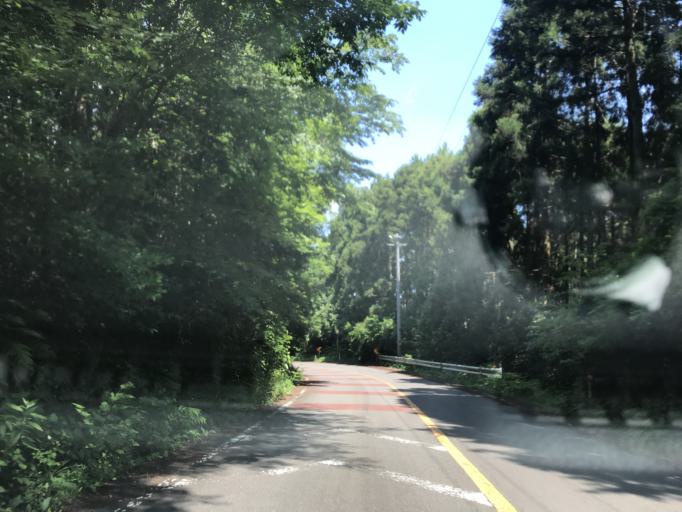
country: JP
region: Miyagi
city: Matsushima
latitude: 38.3658
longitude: 141.0499
